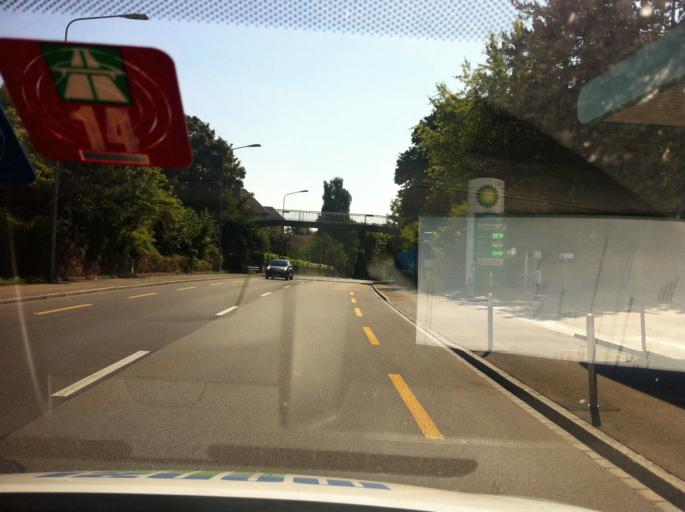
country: CH
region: Zurich
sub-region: Bezirk Horgen
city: Thalwil / Dorfkern
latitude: 47.2866
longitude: 8.5654
